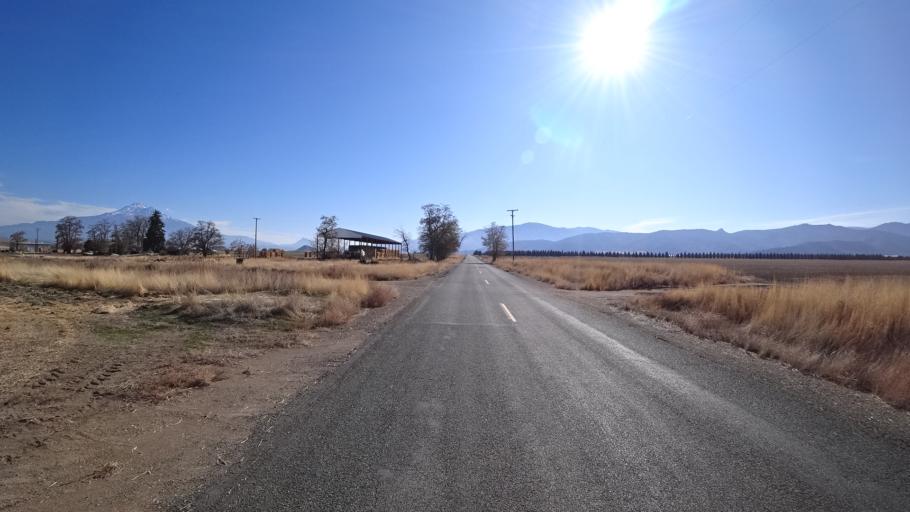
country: US
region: California
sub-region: Siskiyou County
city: Montague
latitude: 41.5602
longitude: -122.5471
